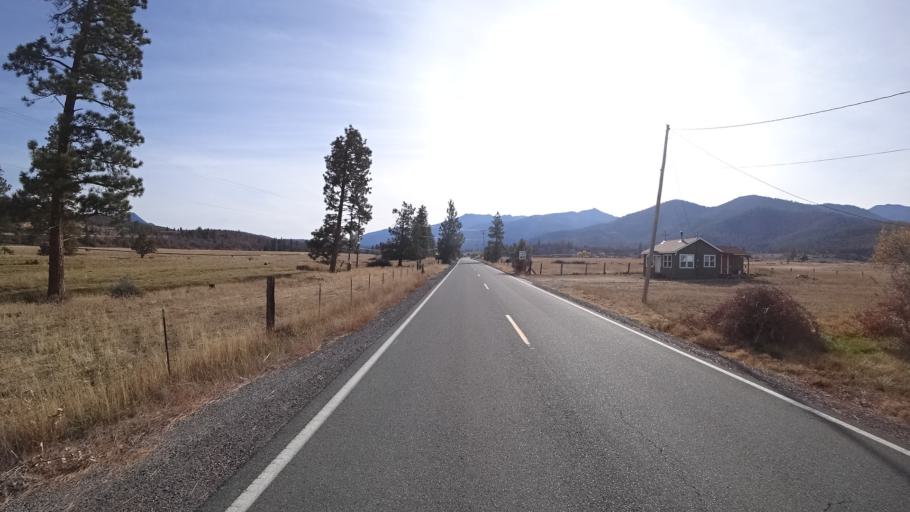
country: US
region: California
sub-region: Siskiyou County
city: Weed
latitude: 41.4383
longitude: -122.4356
